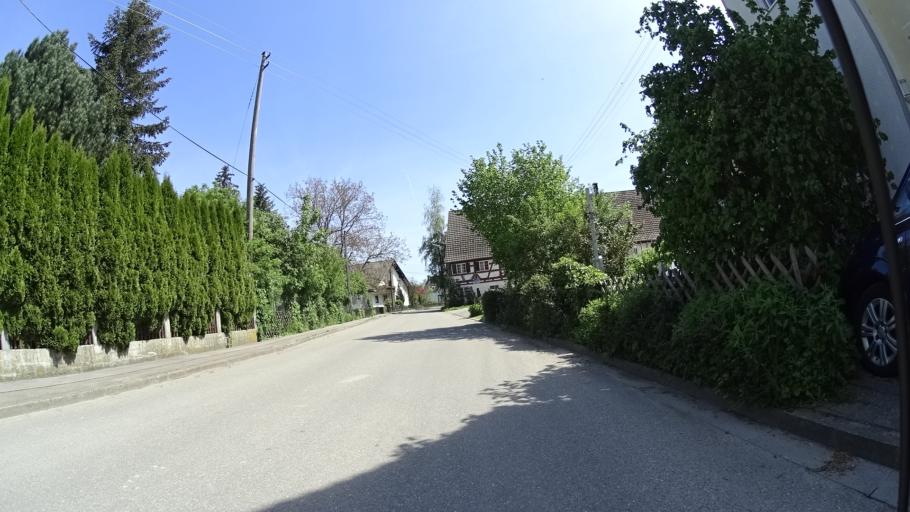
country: DE
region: Bavaria
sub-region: Swabia
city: Pfaffenhofen an der Roth
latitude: 48.3397
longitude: 10.1564
